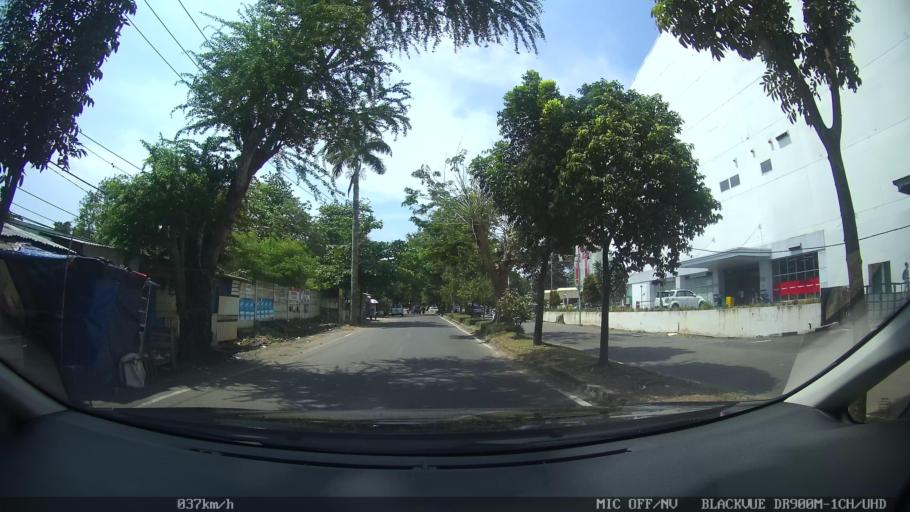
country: ID
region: Lampung
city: Kedaton
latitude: -5.3841
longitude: 105.2816
